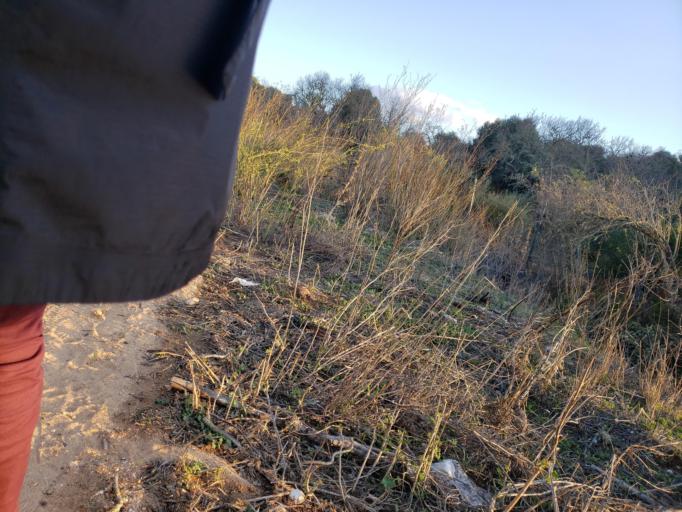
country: PT
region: Faro
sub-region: Portimao
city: Alvor
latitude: 37.1330
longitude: -8.5952
